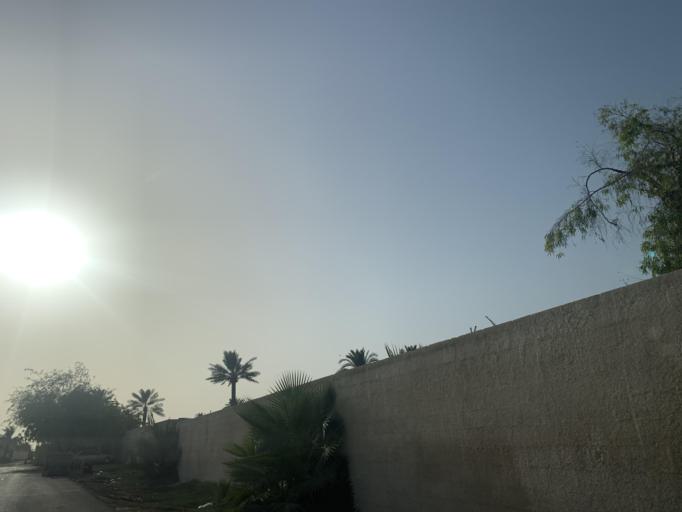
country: BH
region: Central Governorate
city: Madinat Hamad
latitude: 26.1759
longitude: 50.4526
